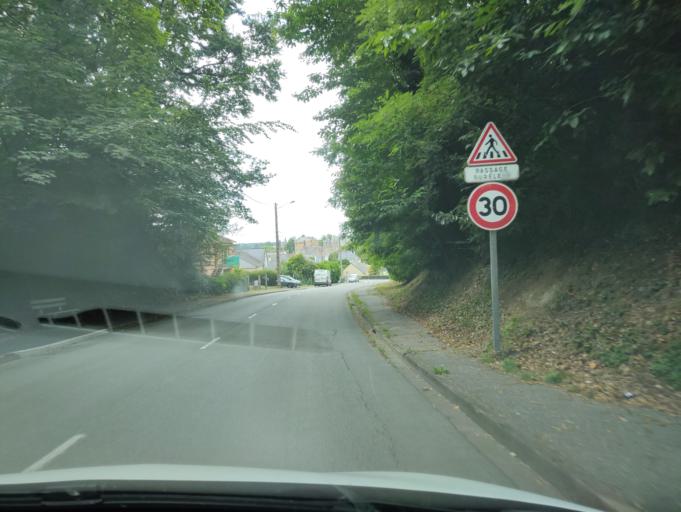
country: FR
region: Pays de la Loire
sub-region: Departement de la Loire-Atlantique
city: Chateaubriant
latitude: 47.7169
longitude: -1.3676
